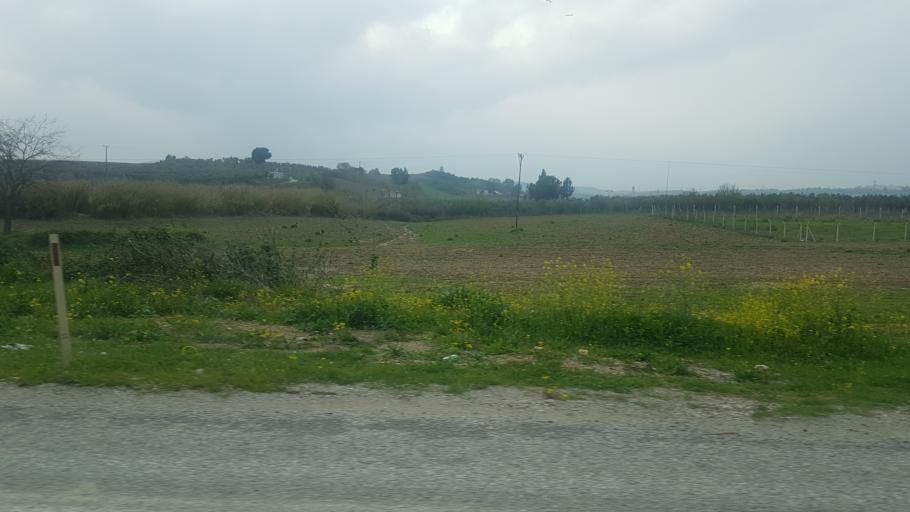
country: TR
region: Mersin
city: Yenice
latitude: 37.0587
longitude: 35.1687
